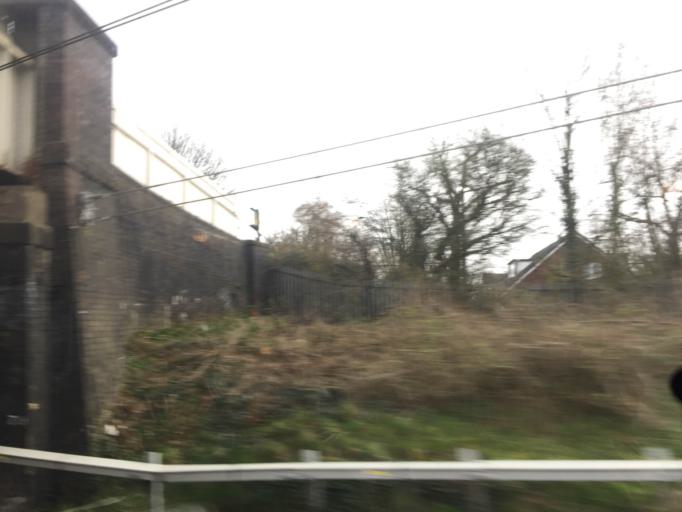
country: GB
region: England
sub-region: Lancashire
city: Coppull
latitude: 53.6133
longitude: -2.6548
